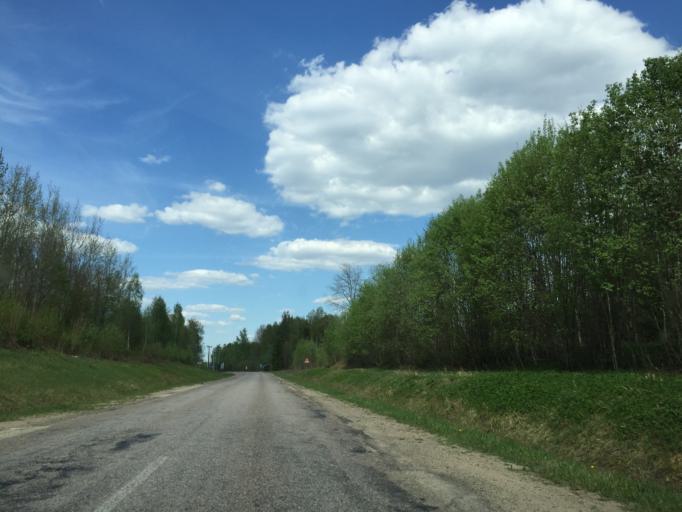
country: LV
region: Limbazu Rajons
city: Limbazi
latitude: 57.4204
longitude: 24.7036
